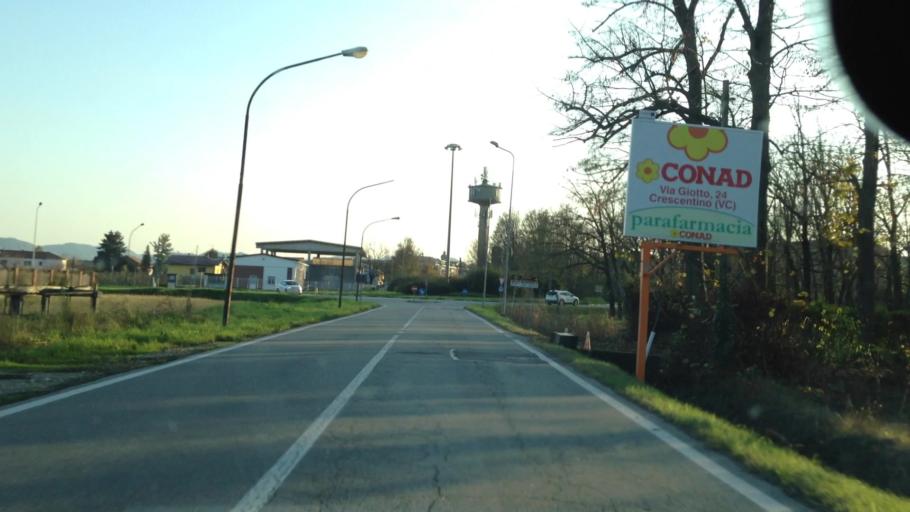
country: IT
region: Piedmont
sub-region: Provincia di Vercelli
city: Crescentino
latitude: 45.1991
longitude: 8.1037
